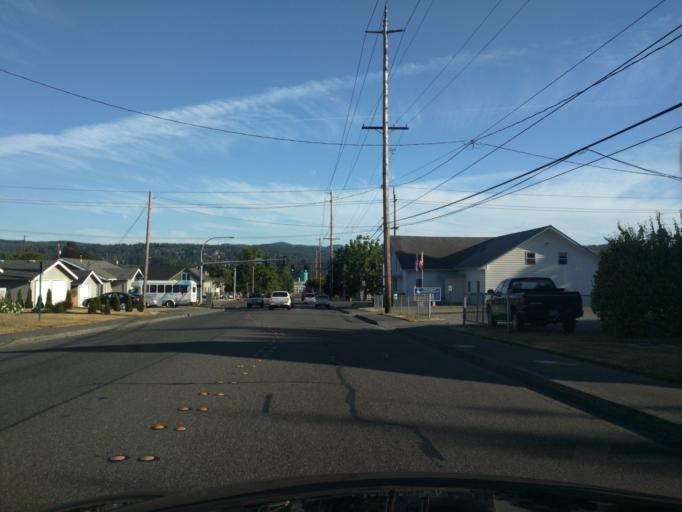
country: US
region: Washington
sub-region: Whatcom County
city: Bellingham
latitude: 48.7638
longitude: -122.4577
